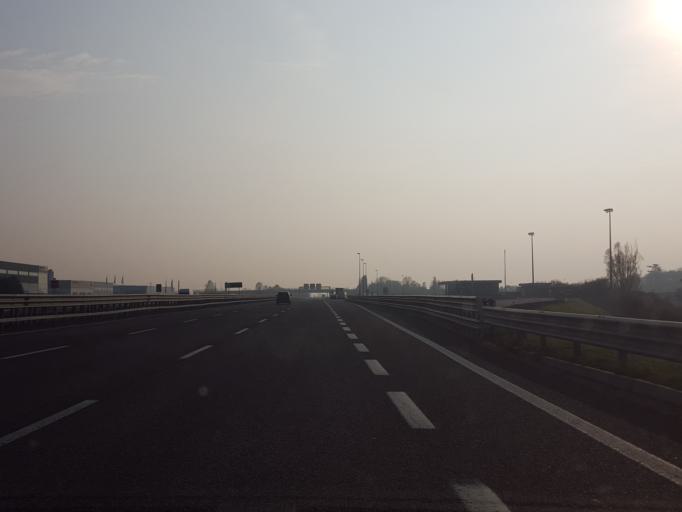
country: IT
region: Veneto
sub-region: Provincia di Treviso
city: Conscio
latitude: 45.5926
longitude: 12.2955
